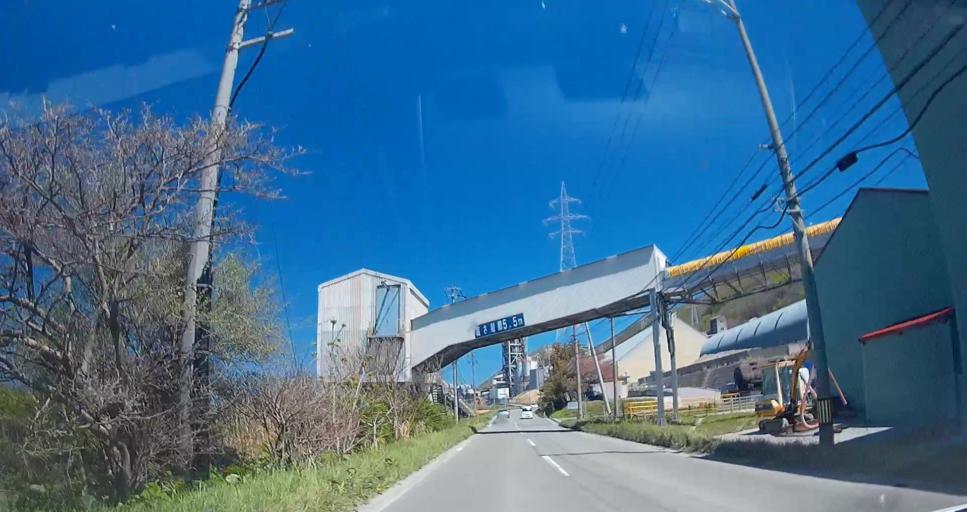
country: JP
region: Aomori
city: Mutsu
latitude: 41.4035
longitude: 141.4305
